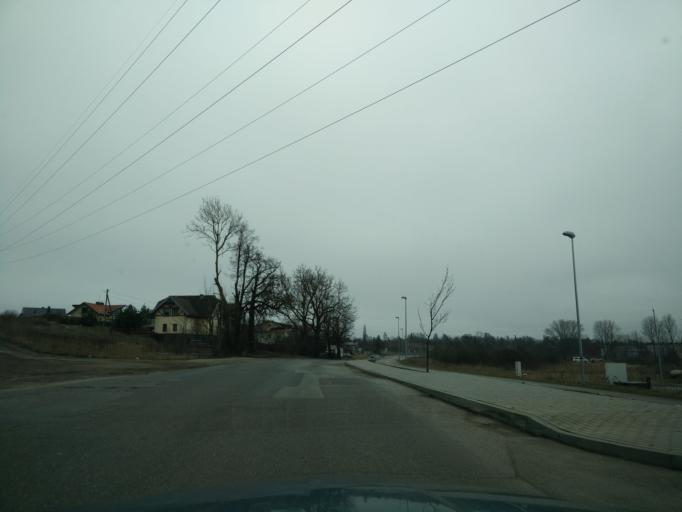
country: LT
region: Klaipedos apskritis
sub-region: Klaipeda
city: Klaipeda
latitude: 55.7220
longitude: 21.1698
